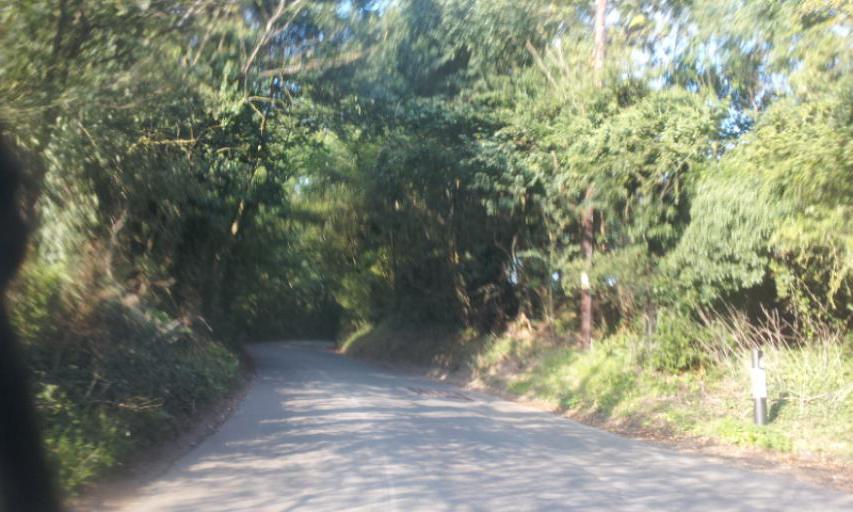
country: GB
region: England
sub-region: Kent
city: Boxley
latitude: 51.2974
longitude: 0.5171
